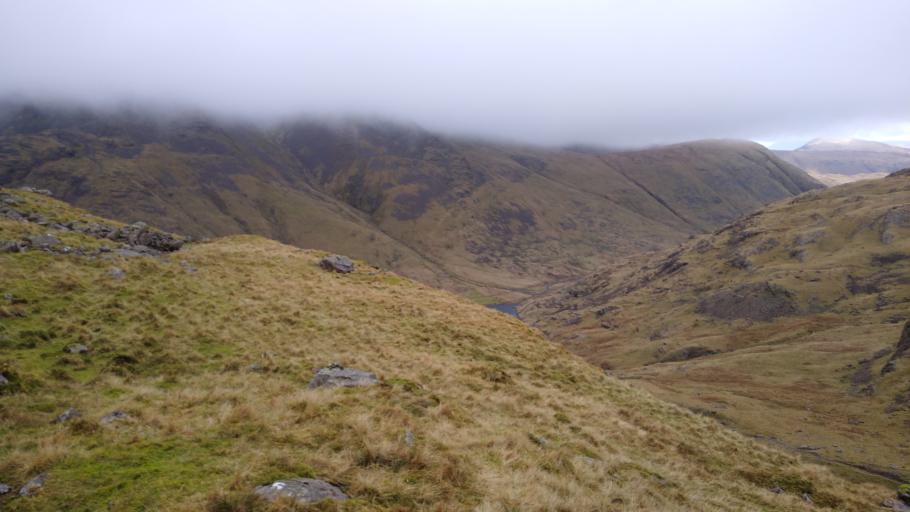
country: GB
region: England
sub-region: Cumbria
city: Keswick
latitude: 54.4714
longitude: -3.1983
